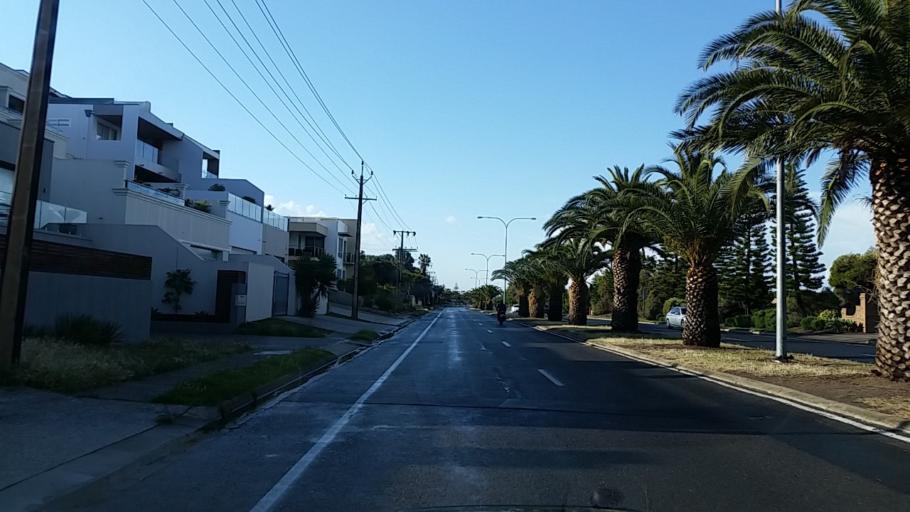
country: AU
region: South Australia
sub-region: Charles Sturt
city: Grange
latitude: -34.8925
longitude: 138.4882
